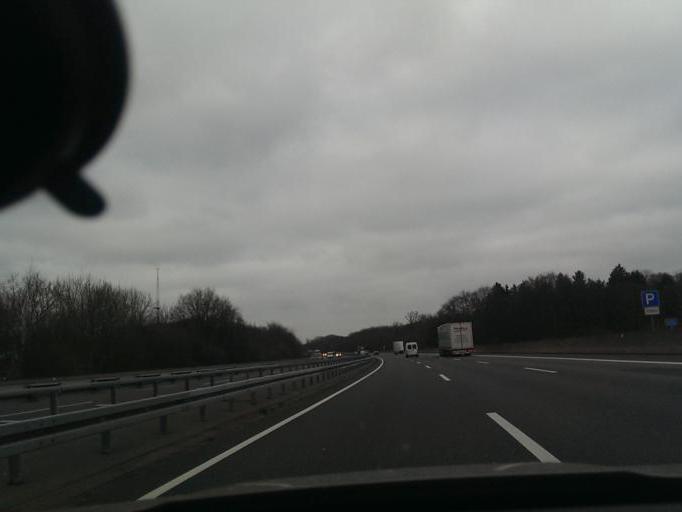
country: DE
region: Lower Saxony
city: Pohle
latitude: 52.2562
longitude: 9.3062
